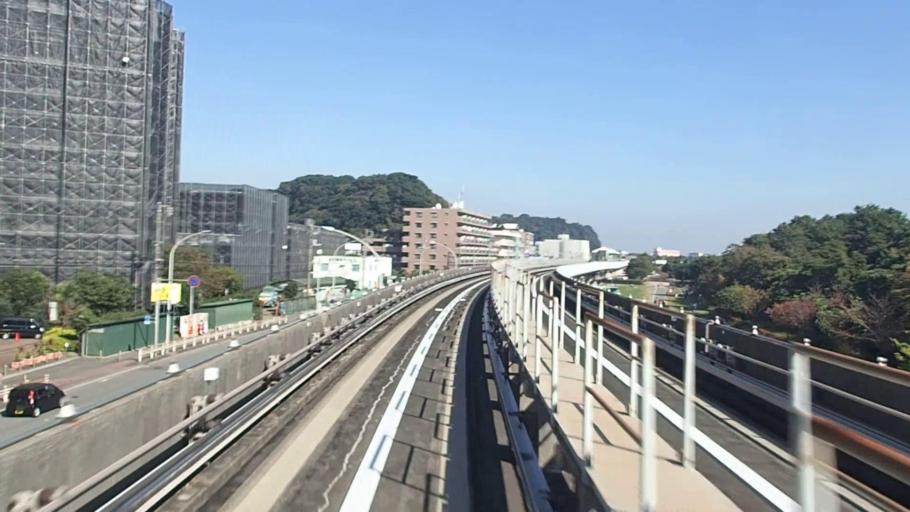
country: JP
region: Kanagawa
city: Yokosuka
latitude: 35.3403
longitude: 139.6339
